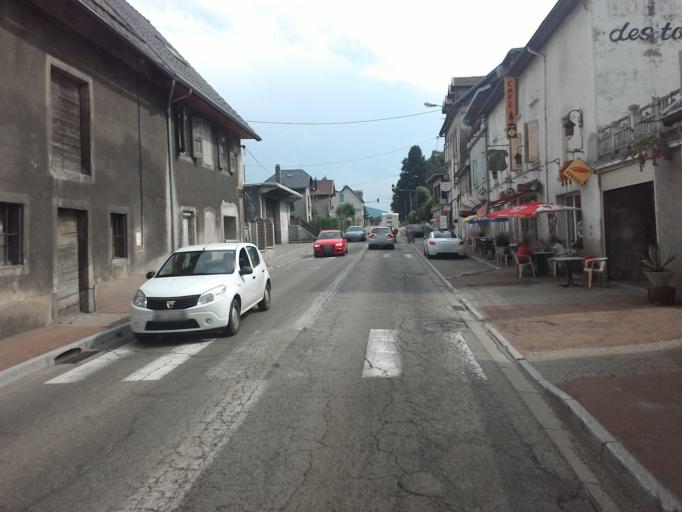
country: FR
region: Rhone-Alpes
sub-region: Departement de l'Isere
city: Notre-Dame-de-Mesage
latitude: 45.0241
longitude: 5.7733
